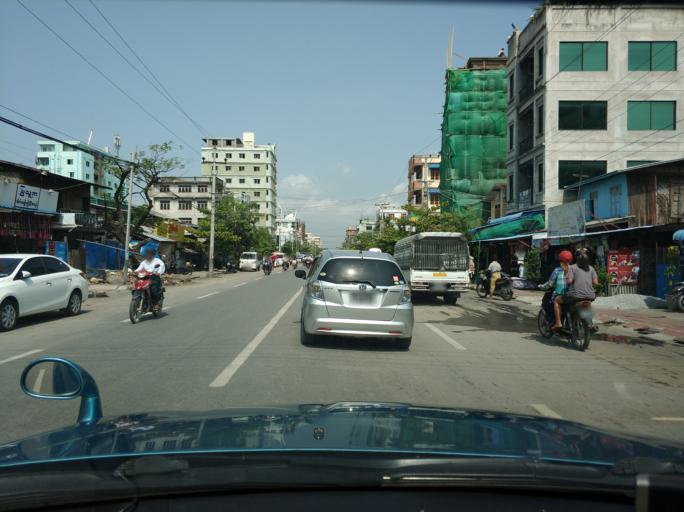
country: MM
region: Mandalay
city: Mandalay
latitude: 21.9658
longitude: 96.0927
